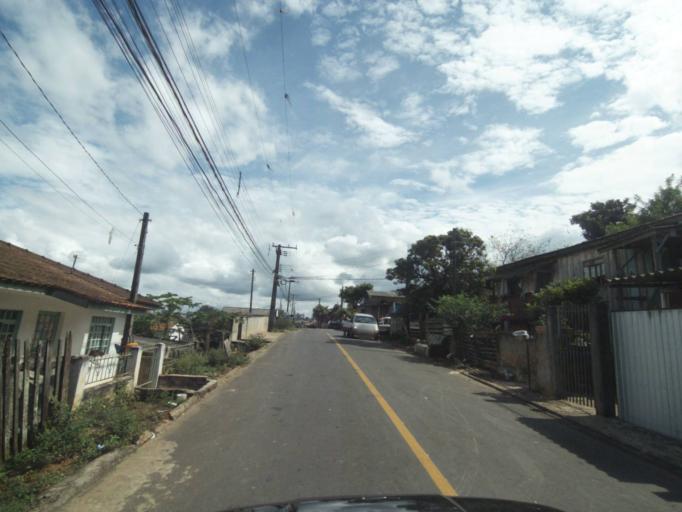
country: BR
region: Parana
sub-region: Telemaco Borba
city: Telemaco Borba
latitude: -24.3173
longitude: -50.6252
